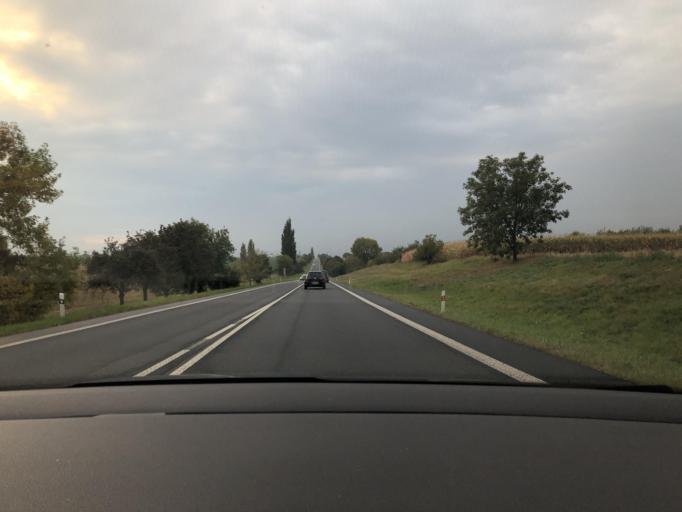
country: CZ
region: Central Bohemia
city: Velim
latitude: 50.0404
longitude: 15.1051
